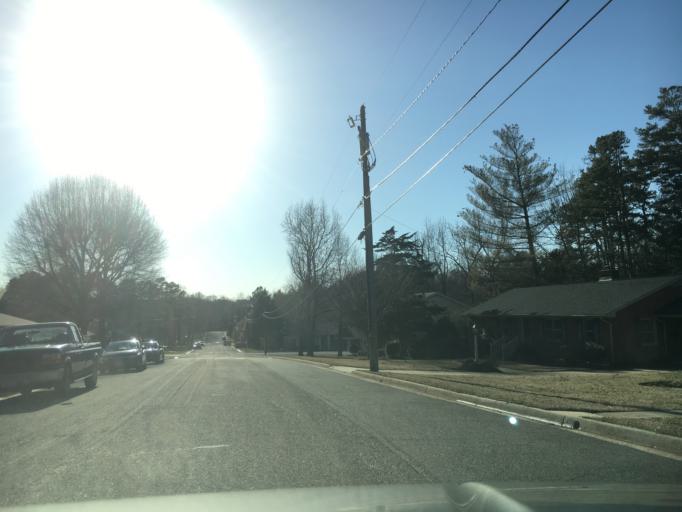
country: US
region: Virginia
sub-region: Halifax County
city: South Boston
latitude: 36.7267
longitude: -78.9079
